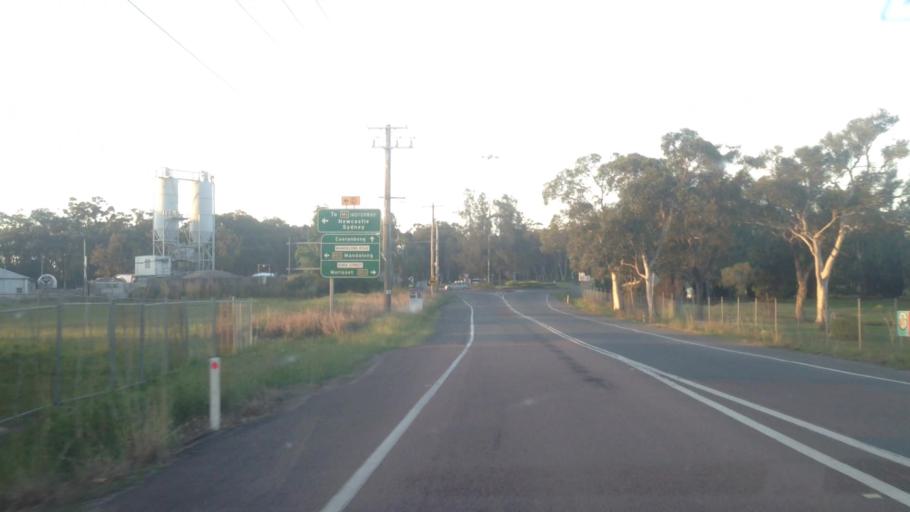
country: AU
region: New South Wales
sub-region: Lake Macquarie Shire
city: Dora Creek
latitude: -33.1146
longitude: 151.4782
